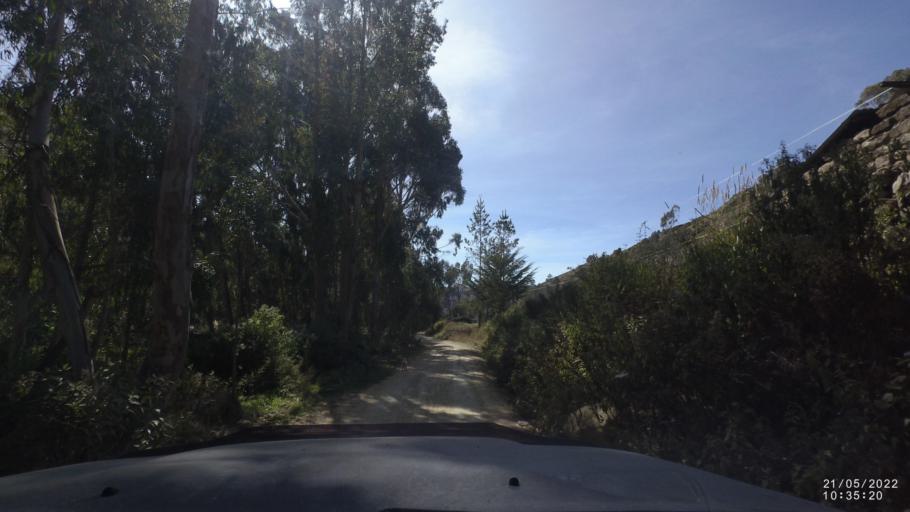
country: BO
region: Cochabamba
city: Colomi
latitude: -17.3182
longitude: -65.9281
